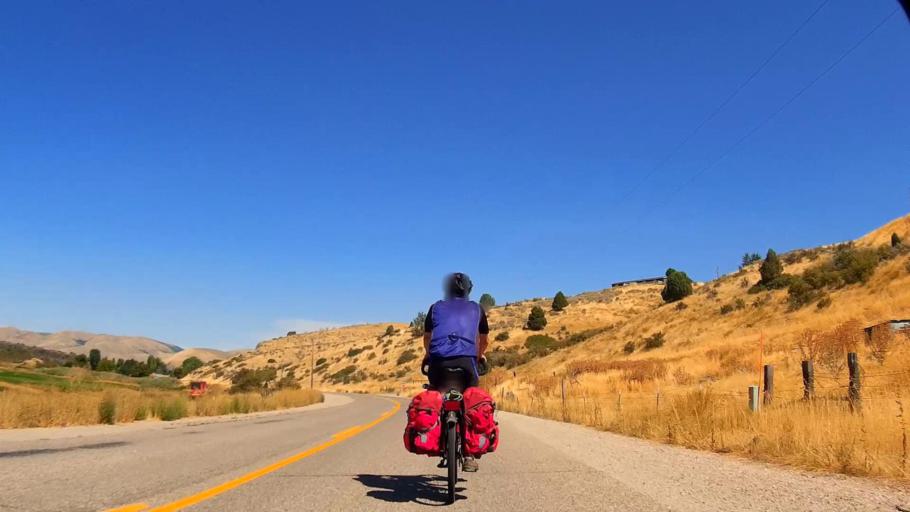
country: US
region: Idaho
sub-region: Bannock County
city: Pocatello
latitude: 42.7591
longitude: -112.2155
